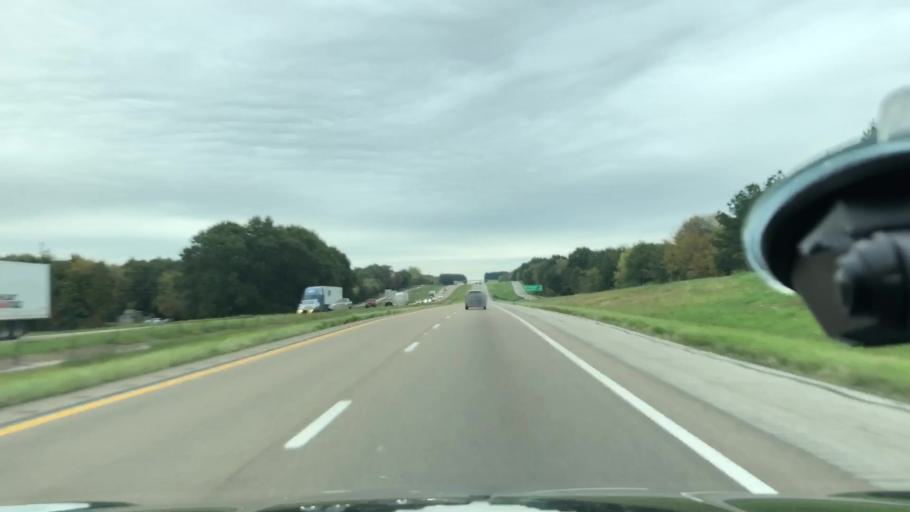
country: US
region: Texas
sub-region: Titus County
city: Mount Pleasant
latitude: 33.1598
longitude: -95.0961
